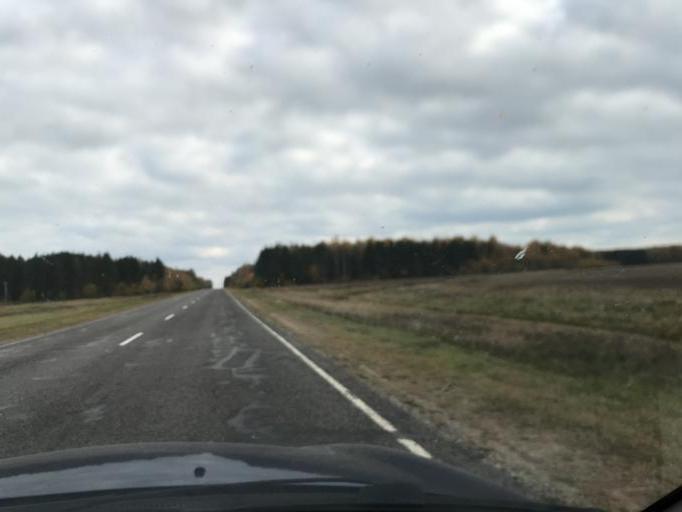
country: BY
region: Grodnenskaya
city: Lida
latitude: 53.7438
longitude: 25.3279
